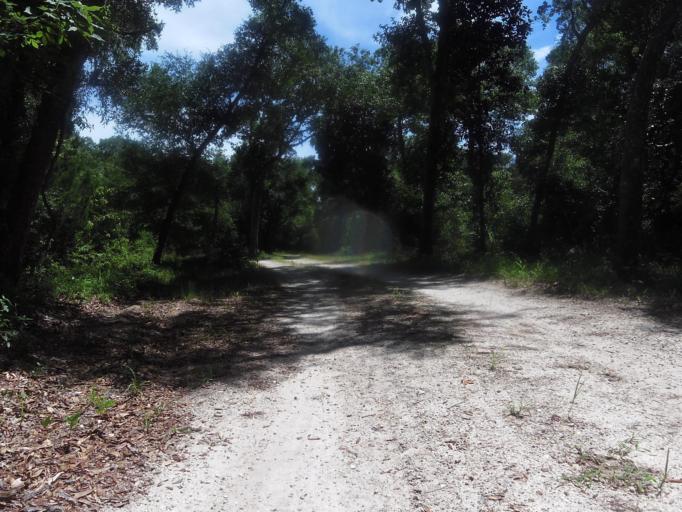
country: US
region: Florida
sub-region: Saint Johns County
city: Villano Beach
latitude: 30.0451
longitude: -81.3385
